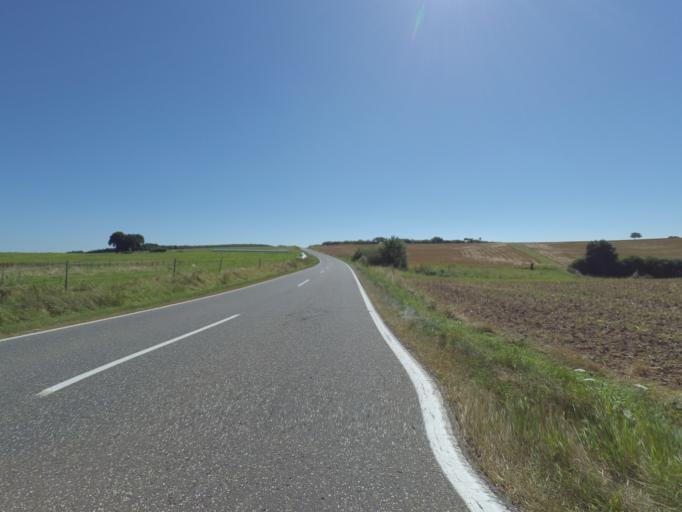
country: DE
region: Rheinland-Pfalz
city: Urschmitt
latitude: 50.1064
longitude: 7.0637
